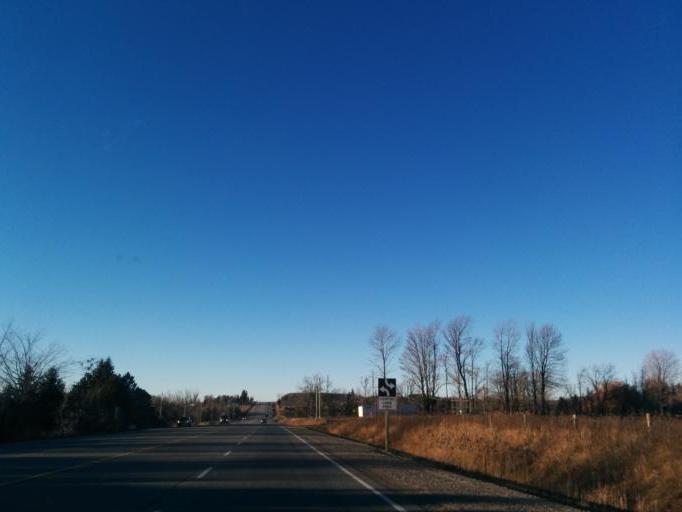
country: CA
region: Ontario
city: Orangeville
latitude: 43.8715
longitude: -80.0108
